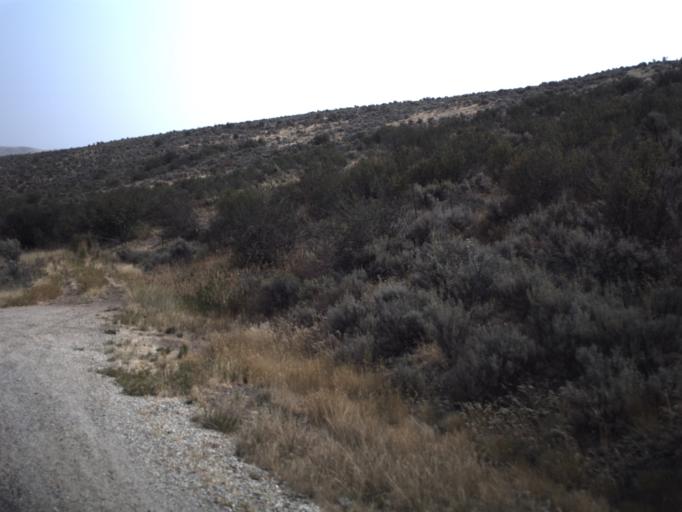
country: US
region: Utah
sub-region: Summit County
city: Coalville
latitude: 40.9724
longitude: -111.5391
